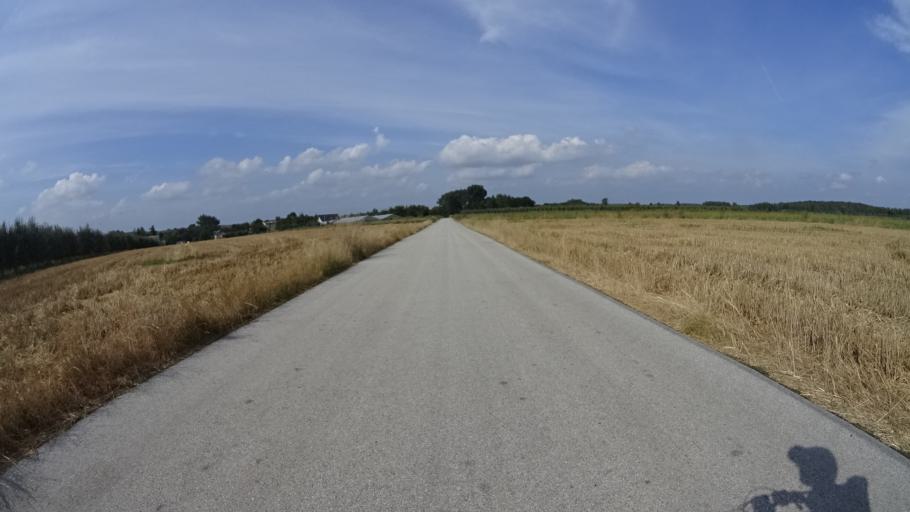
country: PL
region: Masovian Voivodeship
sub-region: Powiat grojecki
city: Goszczyn
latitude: 51.6947
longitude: 20.8474
